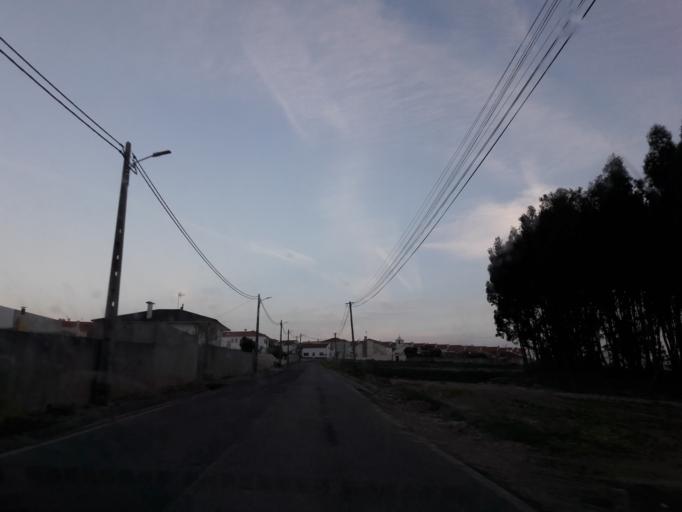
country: PT
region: Leiria
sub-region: Peniche
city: Atouguia da Baleia
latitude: 39.3528
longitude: -9.2930
